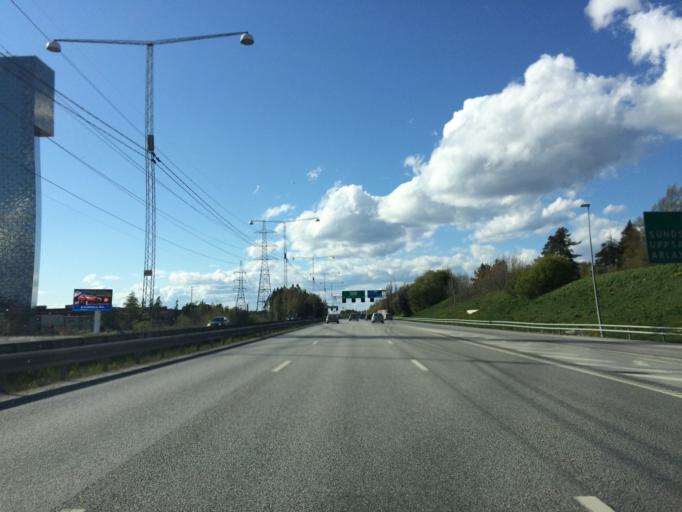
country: SE
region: Stockholm
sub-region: Stockholms Kommun
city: Kista
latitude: 59.4064
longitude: 17.9634
